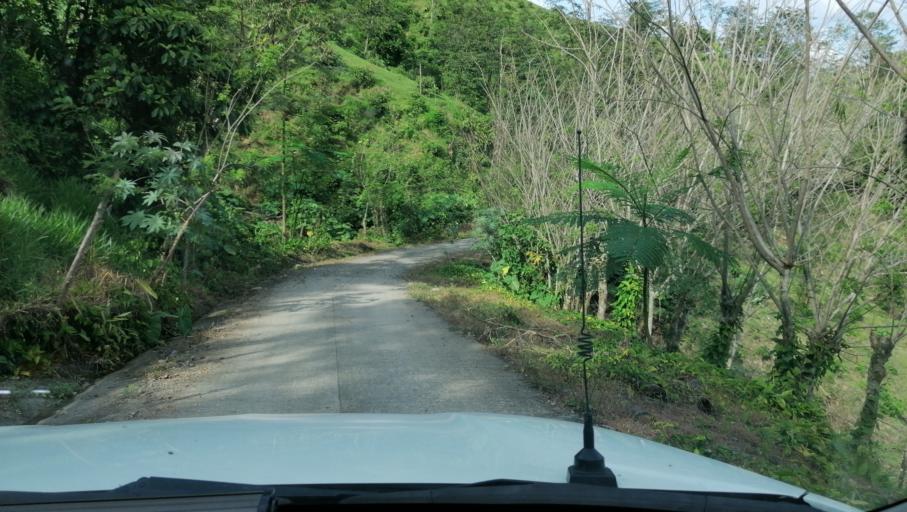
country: MX
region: Chiapas
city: Ostuacan
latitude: 17.4538
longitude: -93.2439
